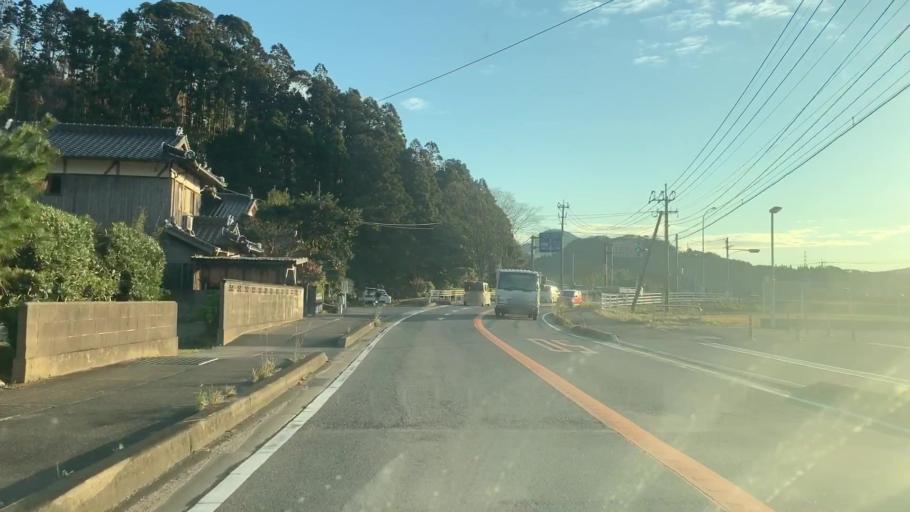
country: JP
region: Saga Prefecture
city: Karatsu
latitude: 33.3558
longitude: 130.0053
